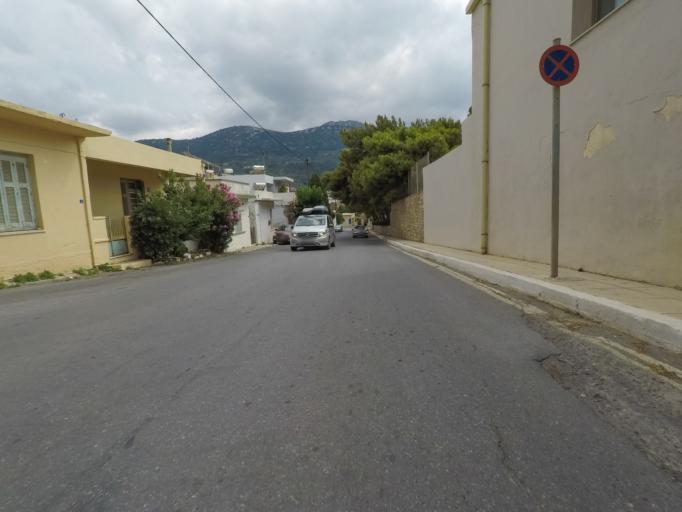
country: GR
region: Crete
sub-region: Nomos Lasithiou
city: Neapoli
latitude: 35.2590
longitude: 25.6083
